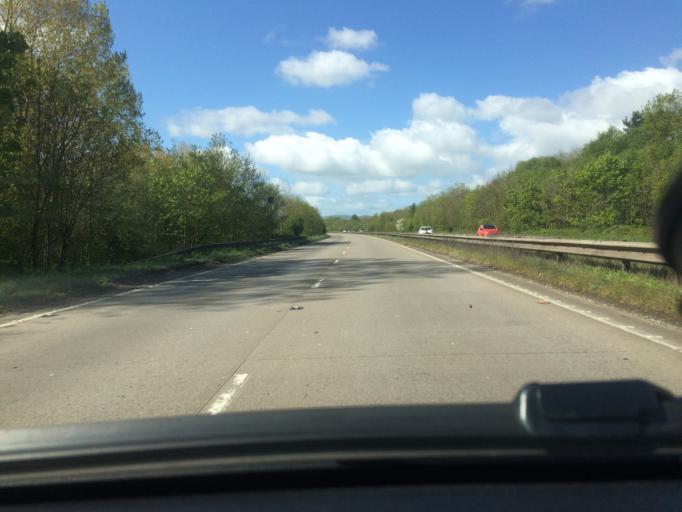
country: GB
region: Wales
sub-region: Wrexham
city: Rossett
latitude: 53.1463
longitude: -2.9302
